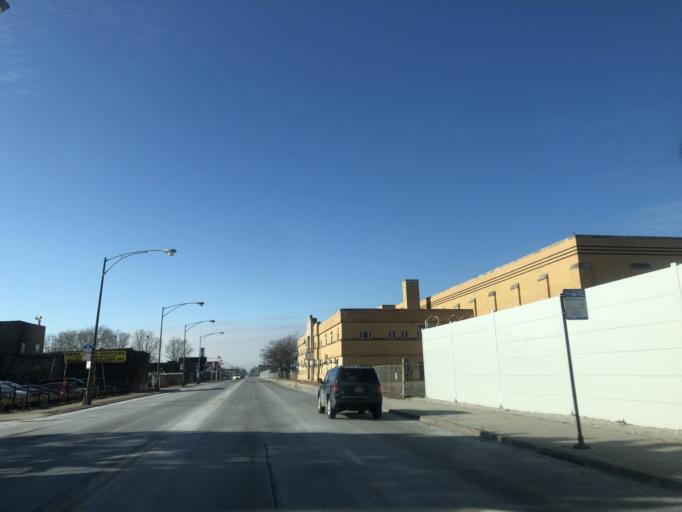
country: US
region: Illinois
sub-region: Cook County
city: Hometown
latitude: 41.7782
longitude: -87.7553
